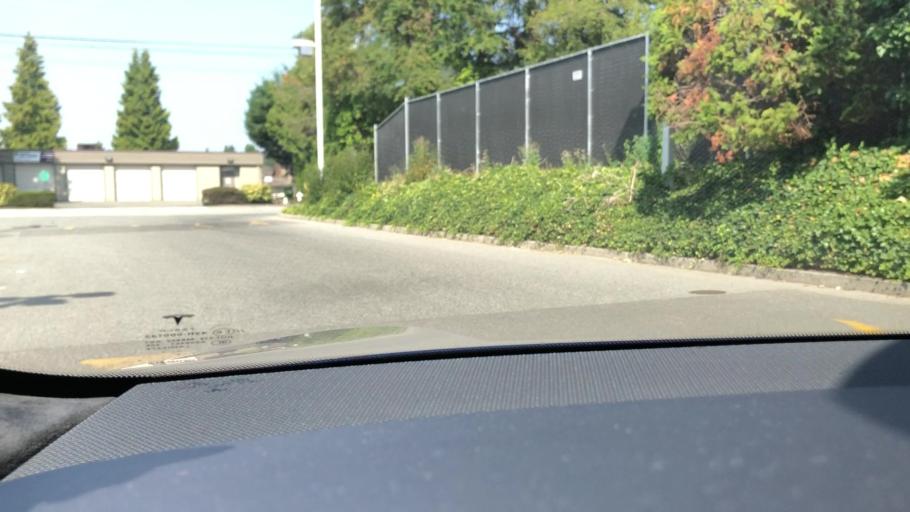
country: US
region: Washington
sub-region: Whatcom County
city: Point Roberts
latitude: 49.0025
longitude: -123.0681
